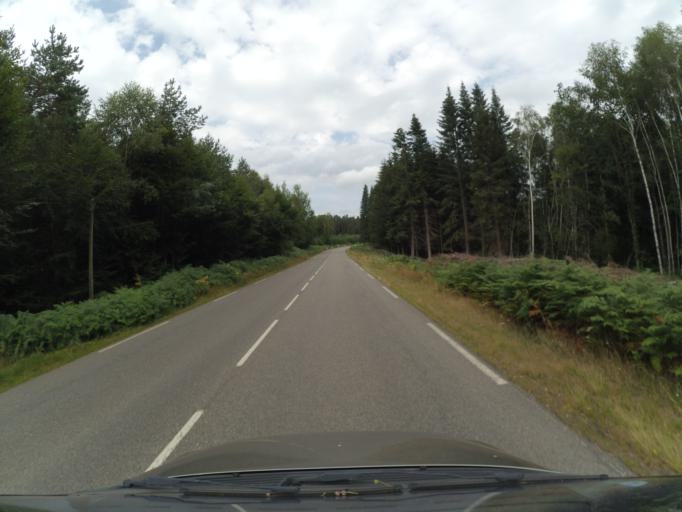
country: FR
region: Limousin
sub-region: Departement de la Correze
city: Ussel
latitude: 45.6166
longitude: 2.2906
